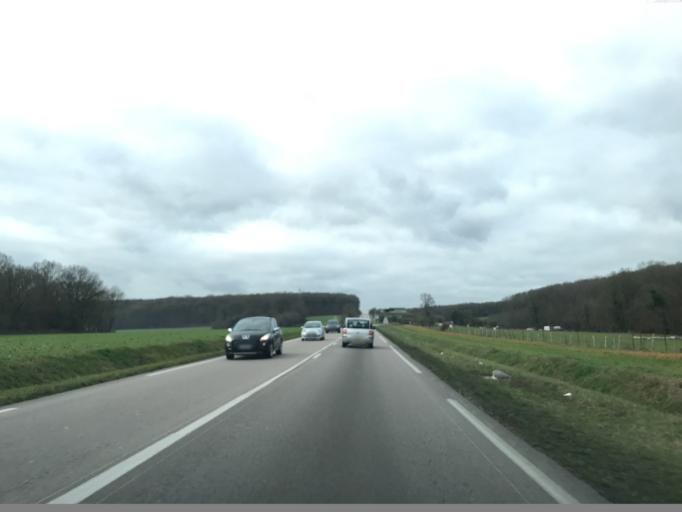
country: FR
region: Haute-Normandie
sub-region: Departement de l'Eure
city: Fleury-sur-Andelle
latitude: 49.3661
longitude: 1.3480
